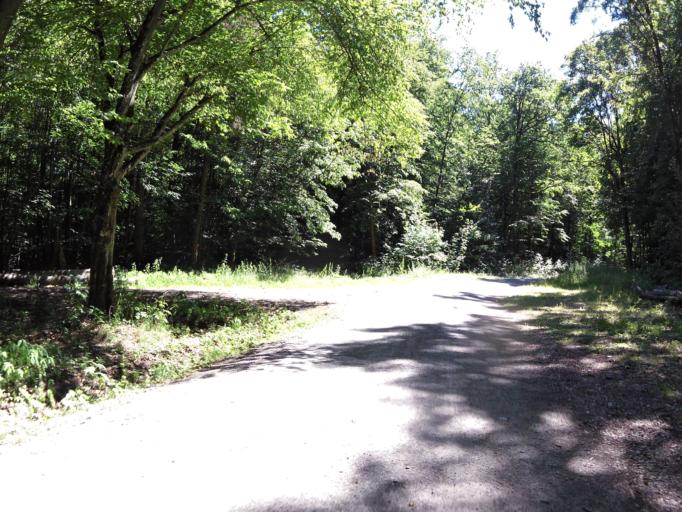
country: DE
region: Bavaria
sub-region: Regierungsbezirk Unterfranken
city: Kleinrinderfeld
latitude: 49.7020
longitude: 9.8678
